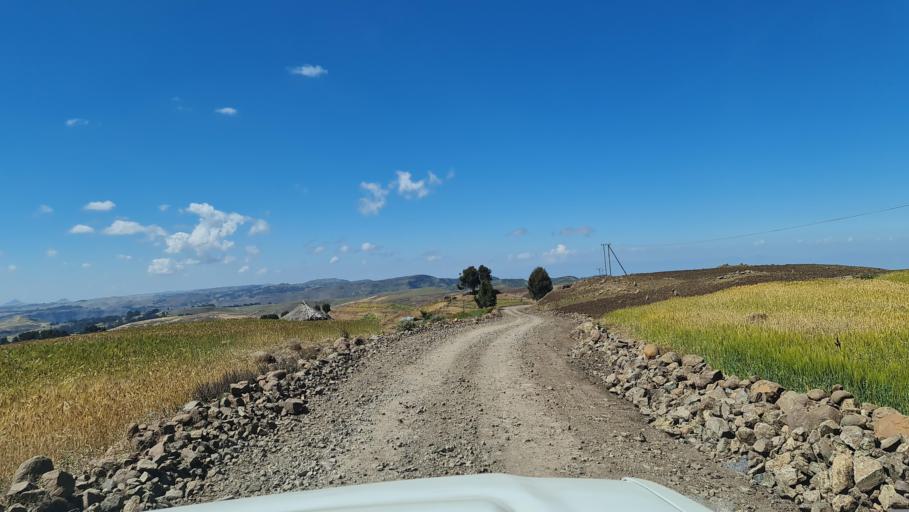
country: ET
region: Amhara
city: Debark'
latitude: 13.2291
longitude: 38.0943
